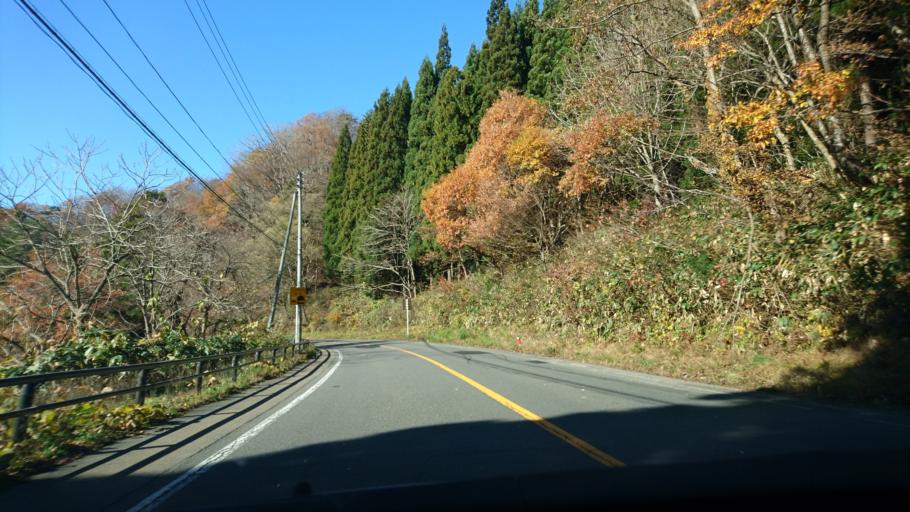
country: JP
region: Akita
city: Yokotemachi
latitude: 39.2823
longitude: 140.6728
